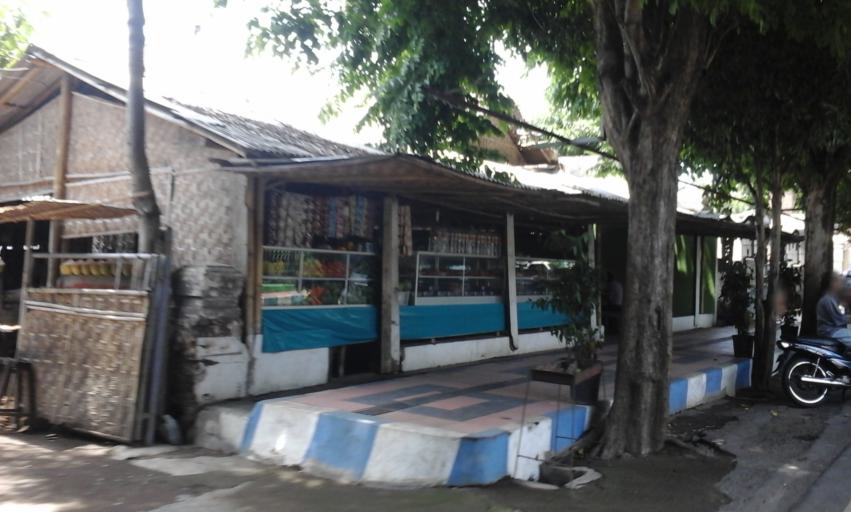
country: ID
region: East Java
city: Banyuwangi
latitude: -8.2166
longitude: 114.3614
